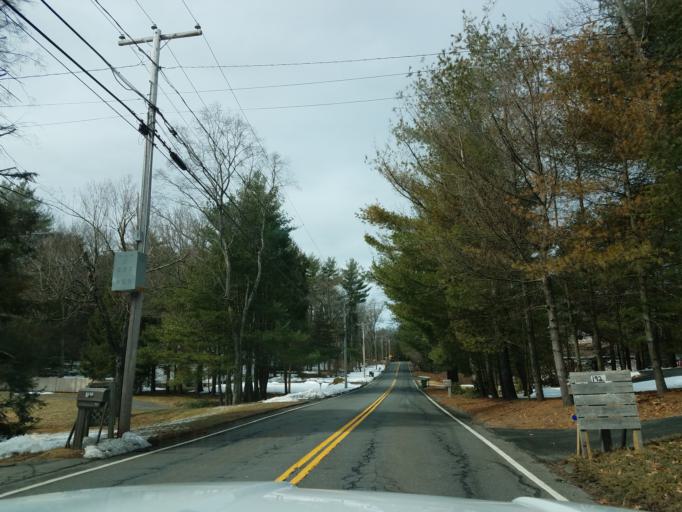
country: US
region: Connecticut
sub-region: Hartford County
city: Weatogue
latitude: 41.8020
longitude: -72.8510
